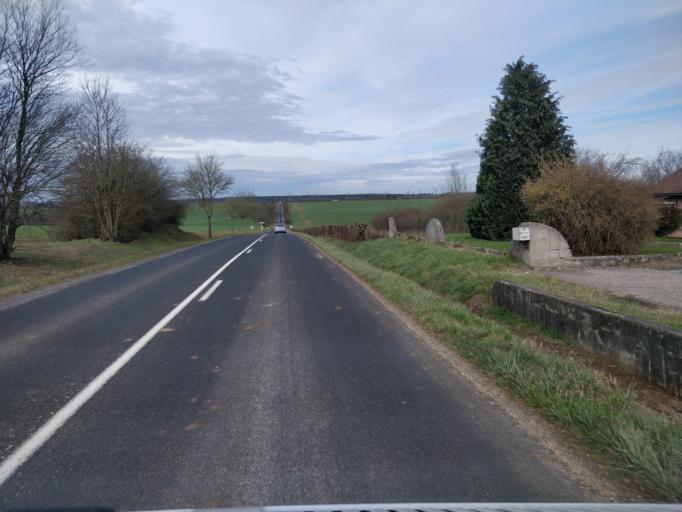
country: FR
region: Lorraine
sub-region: Departement de Meurthe-et-Moselle
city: Montauville
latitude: 48.9015
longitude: 5.9577
